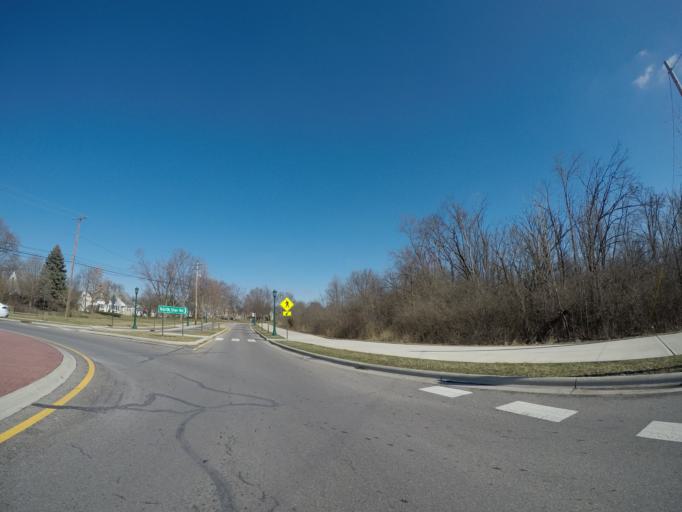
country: US
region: Ohio
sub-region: Franklin County
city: Upper Arlington
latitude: 39.9989
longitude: -83.0479
